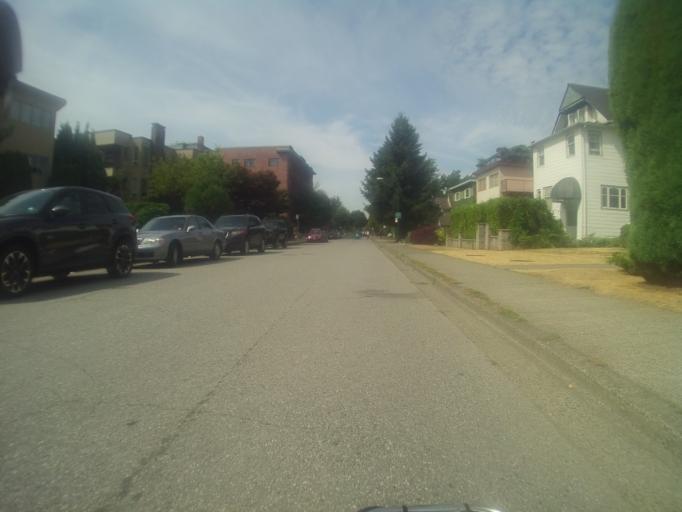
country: CA
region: British Columbia
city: Vancouver
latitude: 49.2626
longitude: -123.1325
